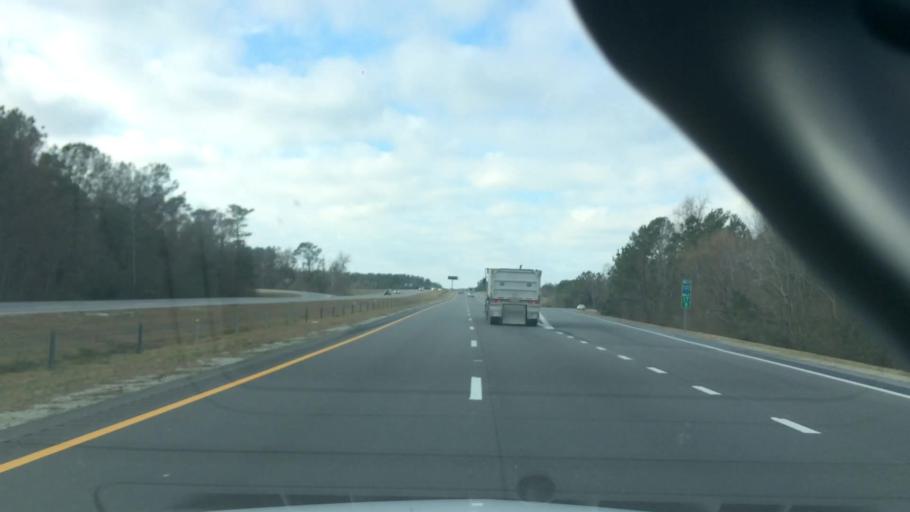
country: US
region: North Carolina
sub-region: New Hanover County
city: Wrightsboro
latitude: 34.3159
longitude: -77.9159
